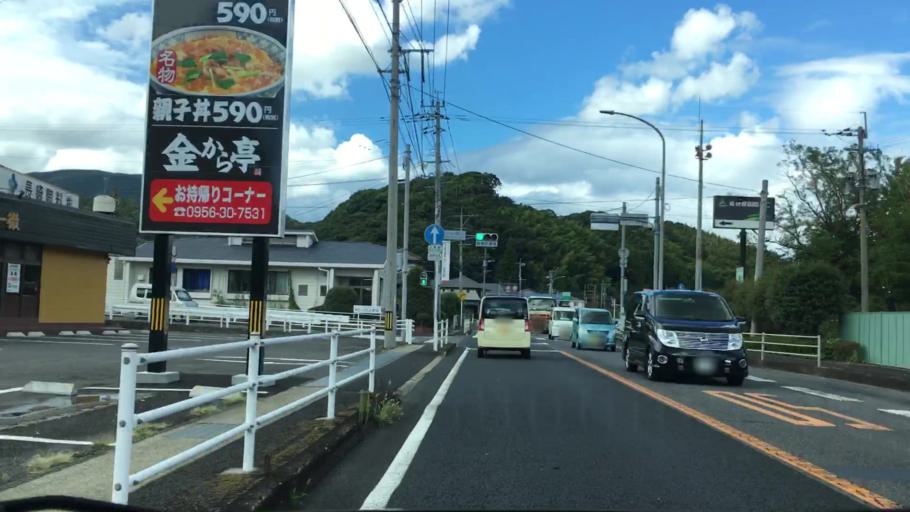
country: JP
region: Nagasaki
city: Sasebo
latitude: 33.1568
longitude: 129.8306
